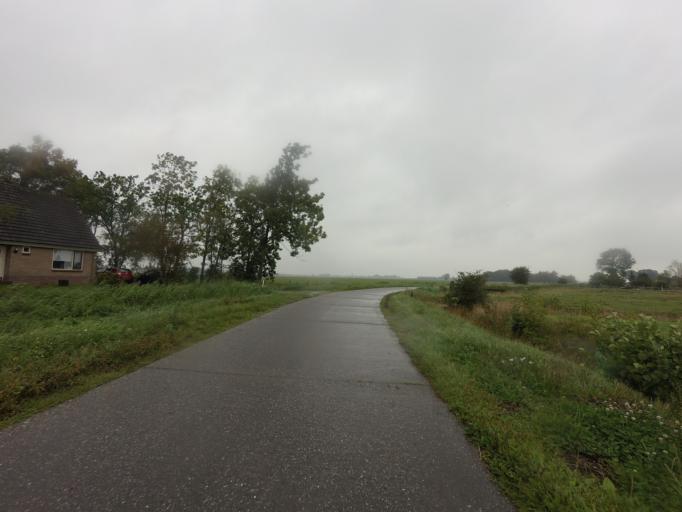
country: NL
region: Friesland
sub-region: Gemeente Boarnsterhim
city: Nes
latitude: 53.0299
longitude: 5.8642
